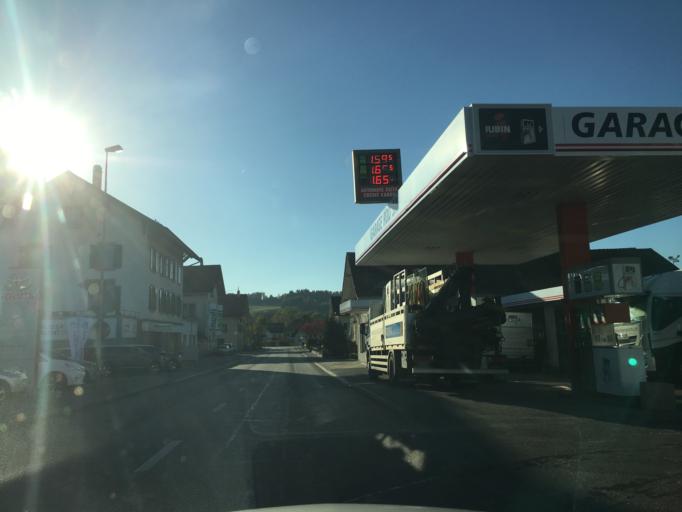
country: CH
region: Vaud
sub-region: Lavaux-Oron District
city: Oron-la-ville
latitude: 46.5710
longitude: 6.8196
